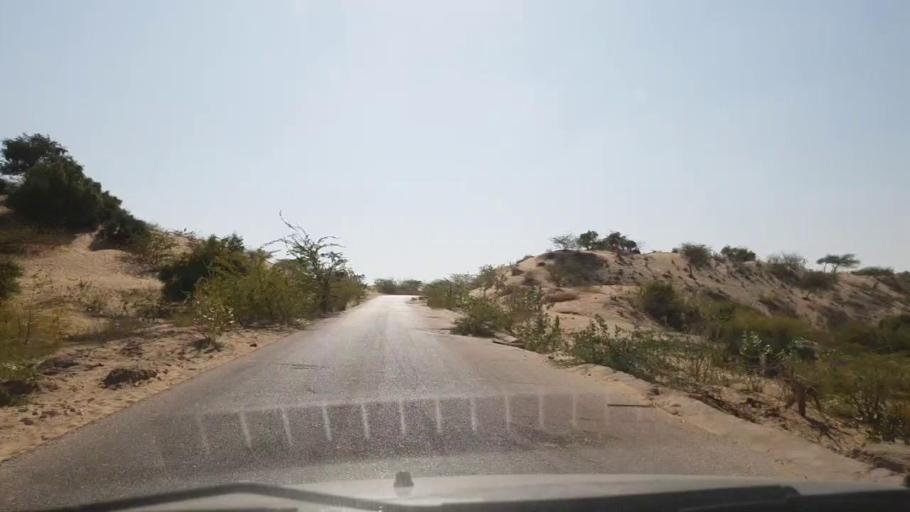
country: PK
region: Sindh
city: Mithi
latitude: 24.5915
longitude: 69.7127
